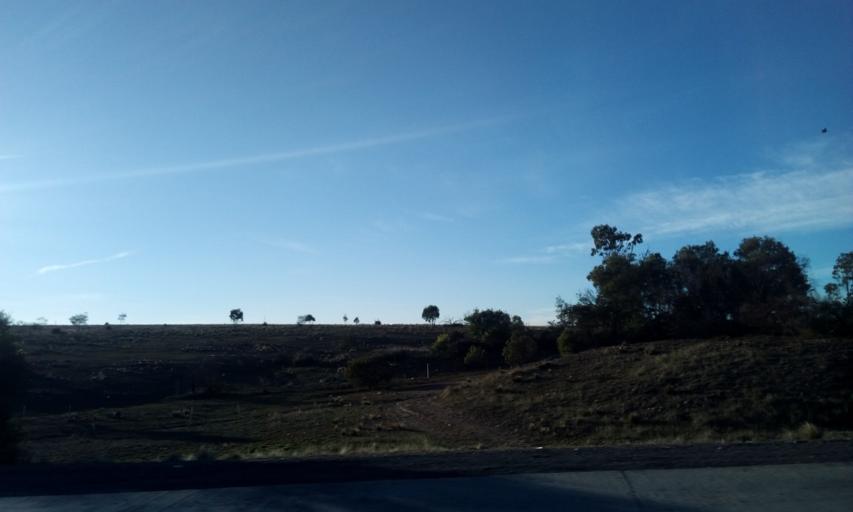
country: AU
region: New South Wales
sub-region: Yass Valley
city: Gundaroo
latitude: -35.1054
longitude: 149.3724
